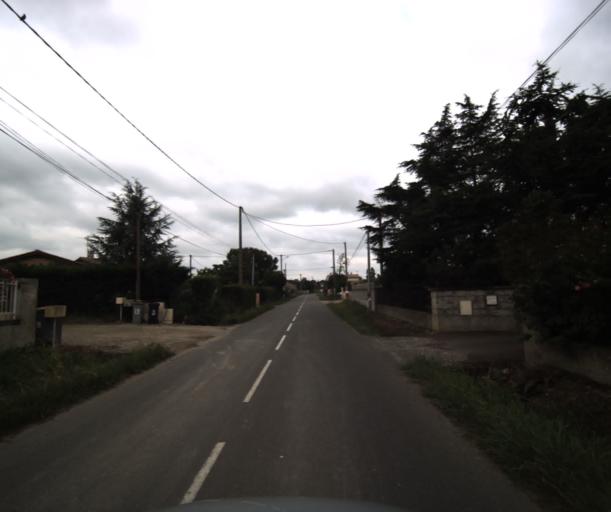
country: FR
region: Midi-Pyrenees
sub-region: Departement de la Haute-Garonne
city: Seysses
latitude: 43.4512
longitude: 1.2993
